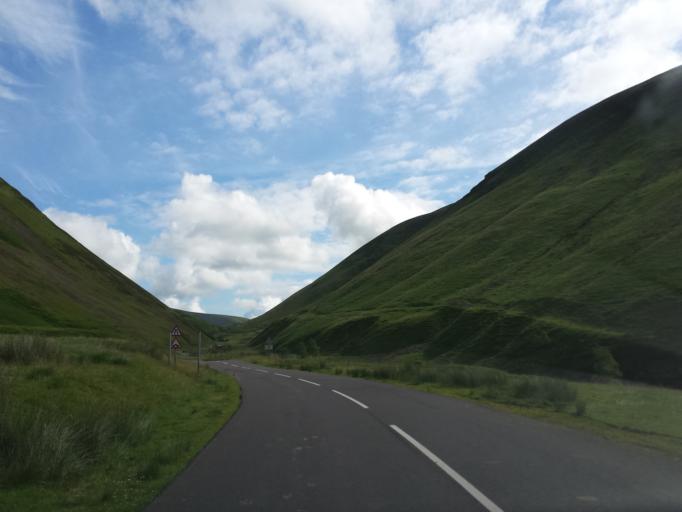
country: GB
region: Scotland
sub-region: Dumfries and Galloway
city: Moffat
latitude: 55.4166
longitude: -3.2881
